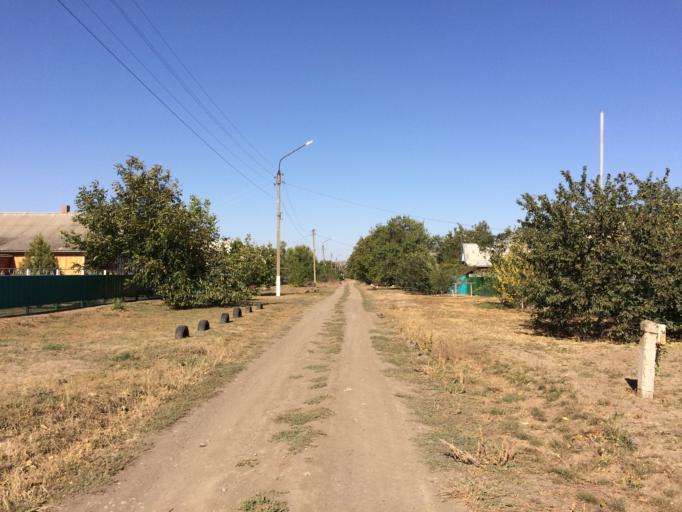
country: RU
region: Rostov
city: Tselina
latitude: 46.5228
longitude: 41.1859
